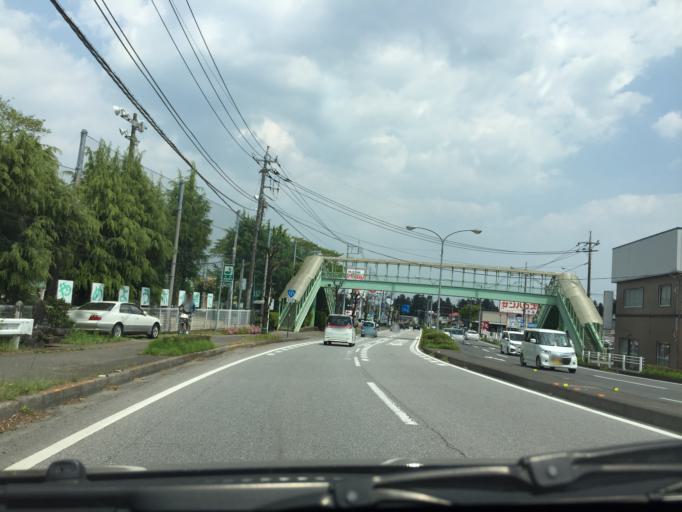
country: JP
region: Tochigi
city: Imaichi
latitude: 36.7334
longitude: 139.6889
